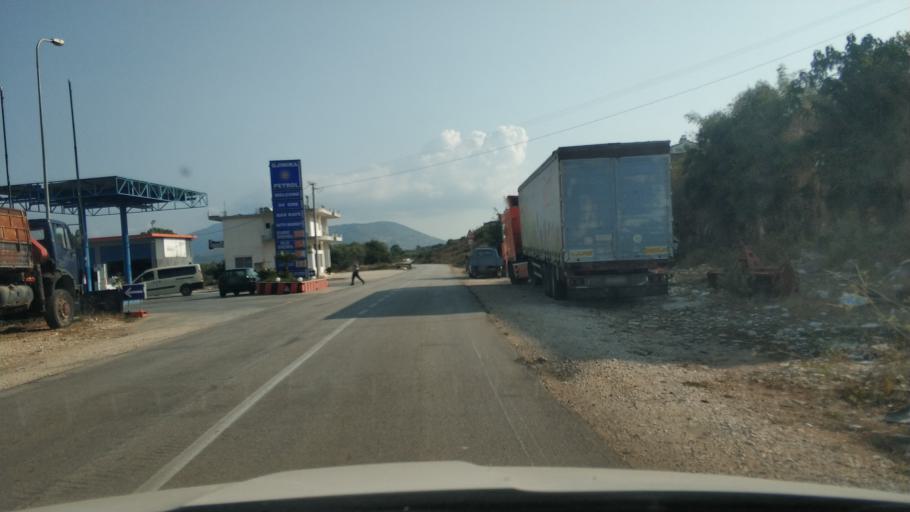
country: AL
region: Vlore
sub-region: Rrethi i Sarandes
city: Sarande
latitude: 39.8494
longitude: 20.0357
